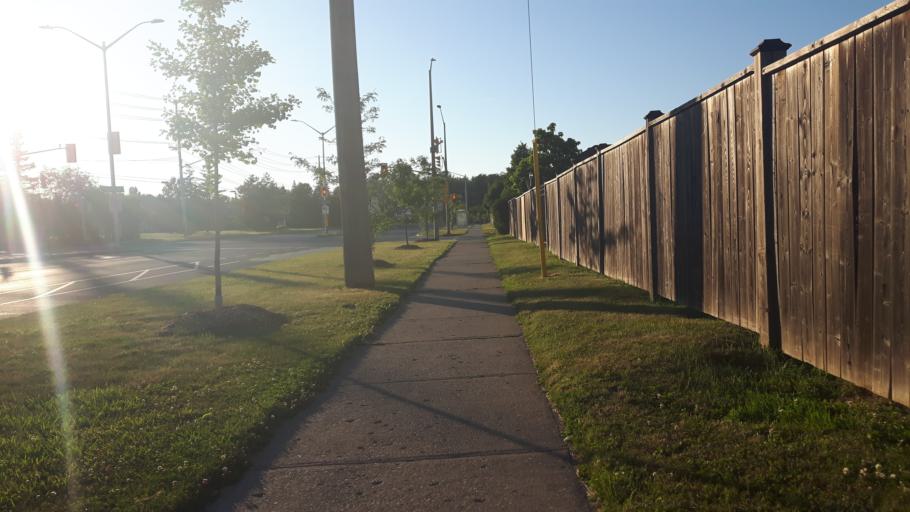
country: CA
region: Ontario
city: London
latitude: 42.9418
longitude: -81.2127
